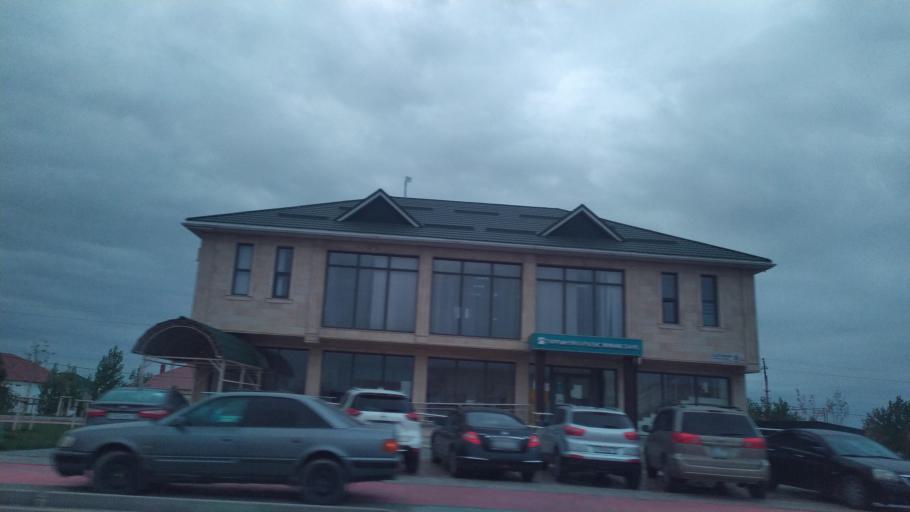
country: KZ
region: Ongtustik Qazaqstan
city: Turkestan
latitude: 43.2793
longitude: 68.3240
